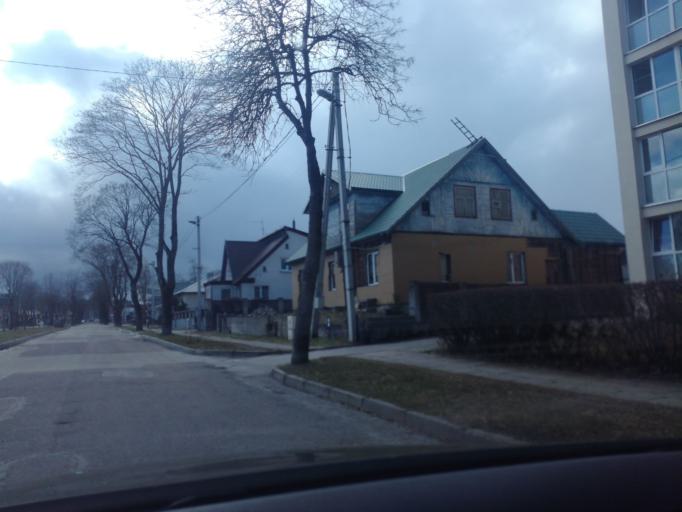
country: LT
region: Alytaus apskritis
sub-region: Alytus
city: Alytus
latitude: 54.3918
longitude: 24.0496
